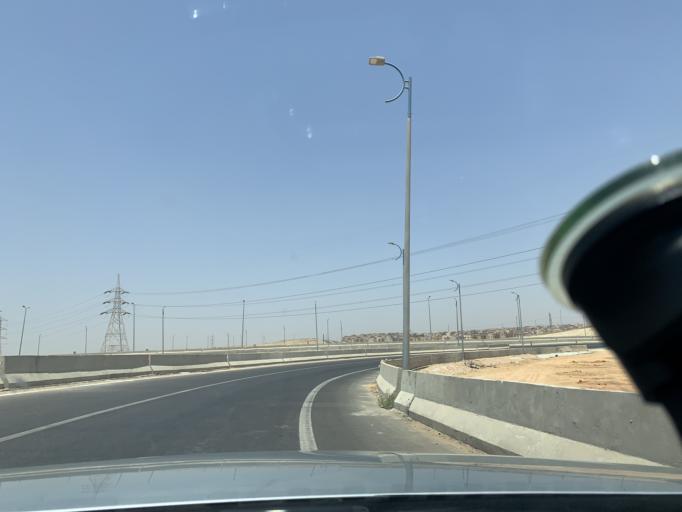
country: EG
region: Muhafazat al Qahirah
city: Halwan
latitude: 29.9657
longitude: 31.4675
